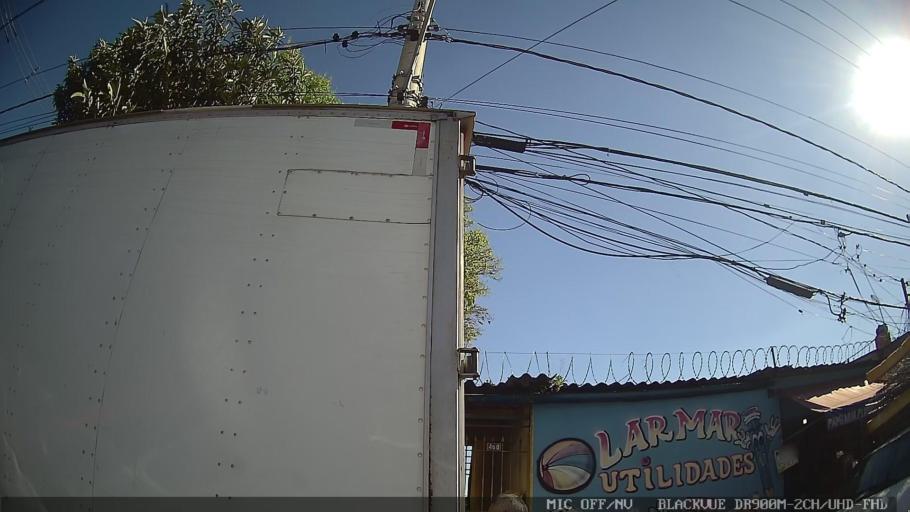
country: BR
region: Sao Paulo
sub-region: Guarulhos
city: Guarulhos
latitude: -23.5444
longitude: -46.4879
